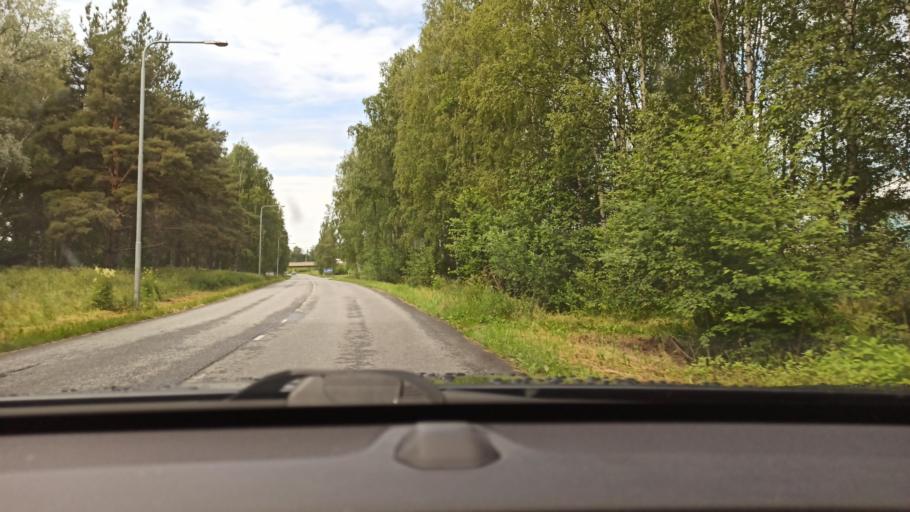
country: FI
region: Satakunta
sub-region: Pori
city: Pori
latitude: 61.5100
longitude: 21.7743
